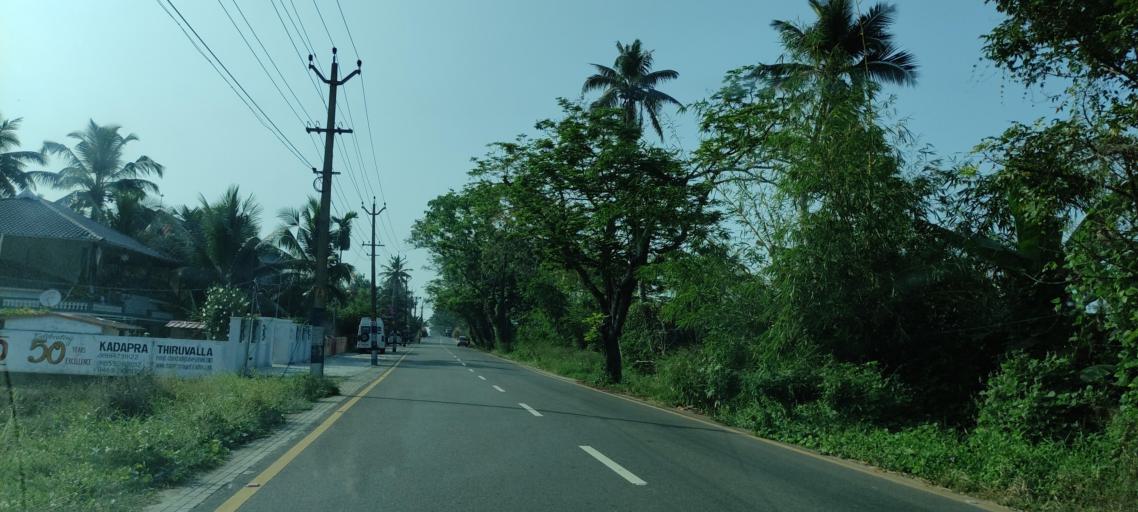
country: IN
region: Kerala
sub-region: Kottayam
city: Changanacheri
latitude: 9.3641
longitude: 76.4436
